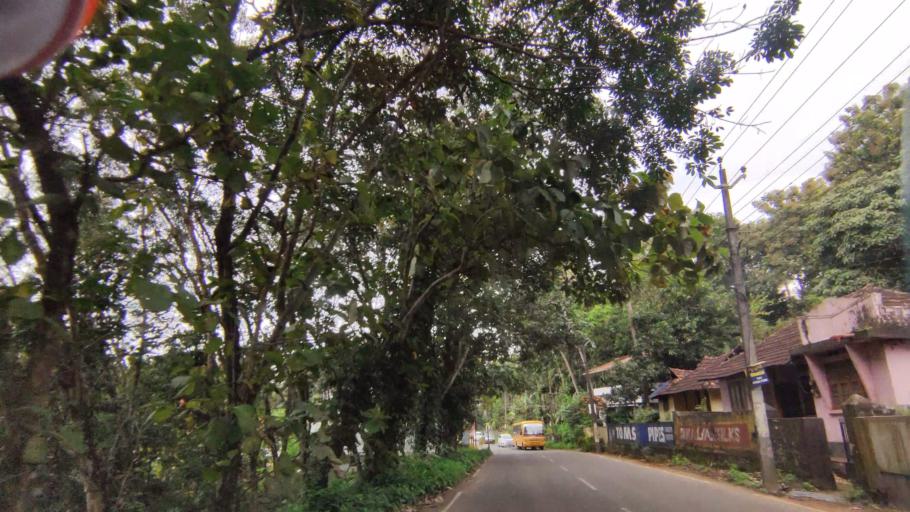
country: IN
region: Kerala
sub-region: Kottayam
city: Kottayam
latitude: 9.6625
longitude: 76.5308
